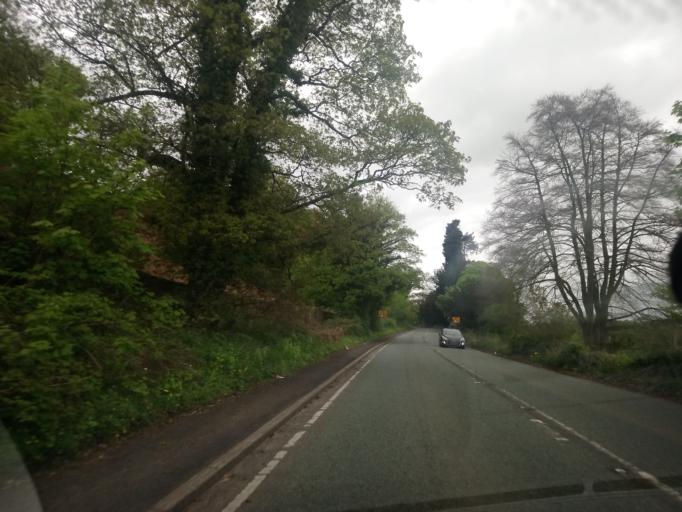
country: GB
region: England
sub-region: Telford and Wrekin
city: Newport
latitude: 52.7872
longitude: -2.3871
